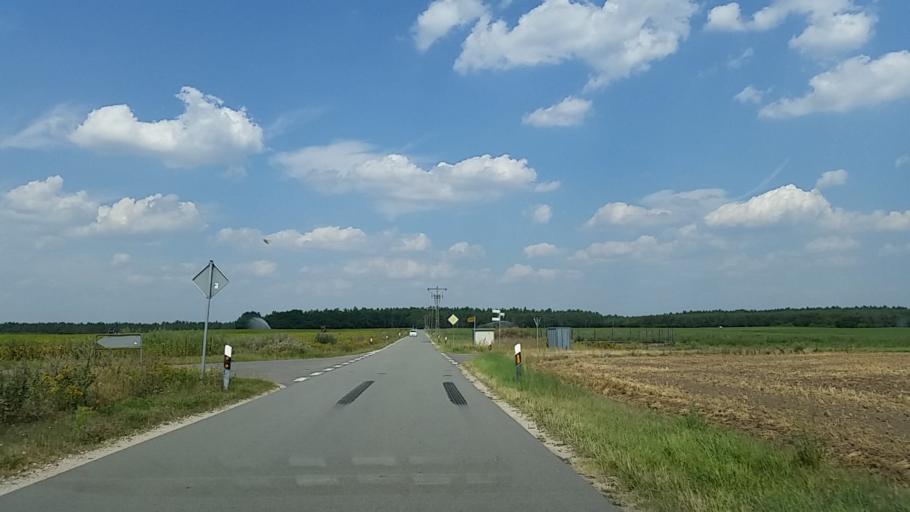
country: DE
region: Lower Saxony
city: Bodenteich
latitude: 52.8008
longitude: 10.7150
